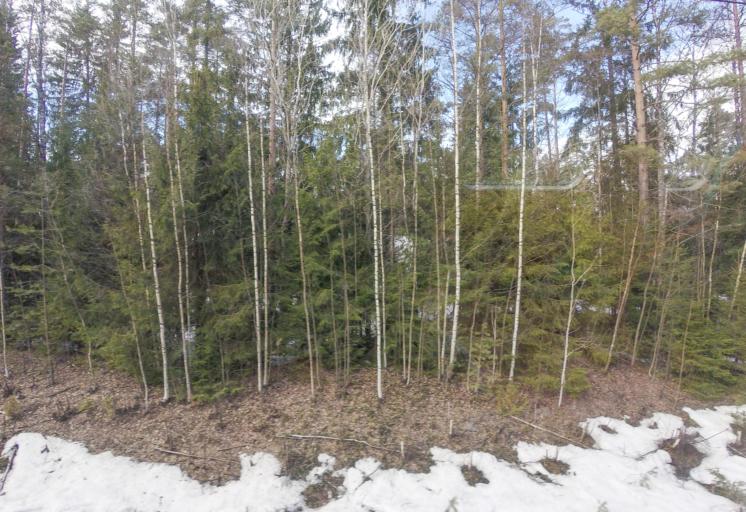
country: FI
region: South Karelia
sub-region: Lappeenranta
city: Joutseno
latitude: 61.1140
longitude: 28.4645
